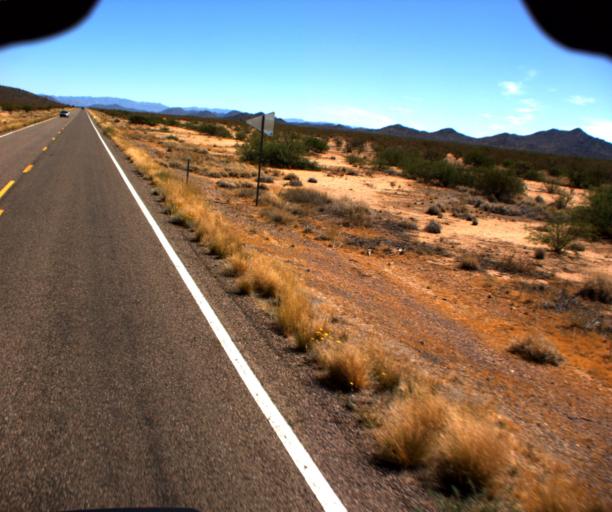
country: US
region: Arizona
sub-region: Yavapai County
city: Congress
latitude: 33.9944
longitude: -113.1288
